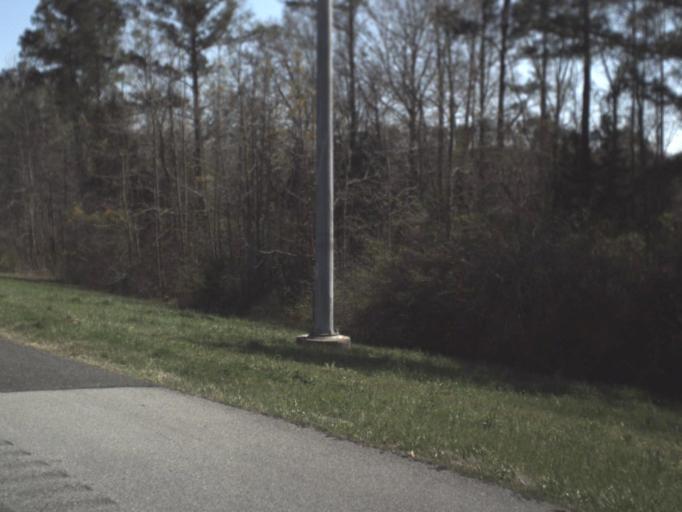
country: US
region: Florida
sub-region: Jackson County
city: Marianna
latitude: 30.7559
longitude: -85.2787
